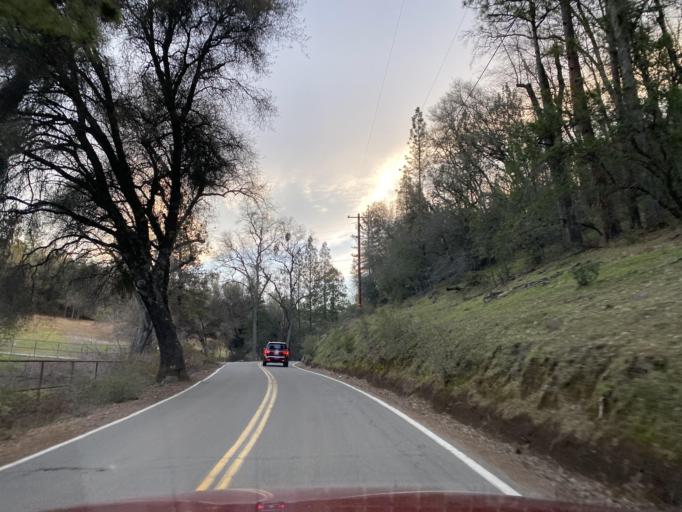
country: US
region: California
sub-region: Amador County
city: Pine Grove
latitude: 38.4983
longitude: -120.7122
